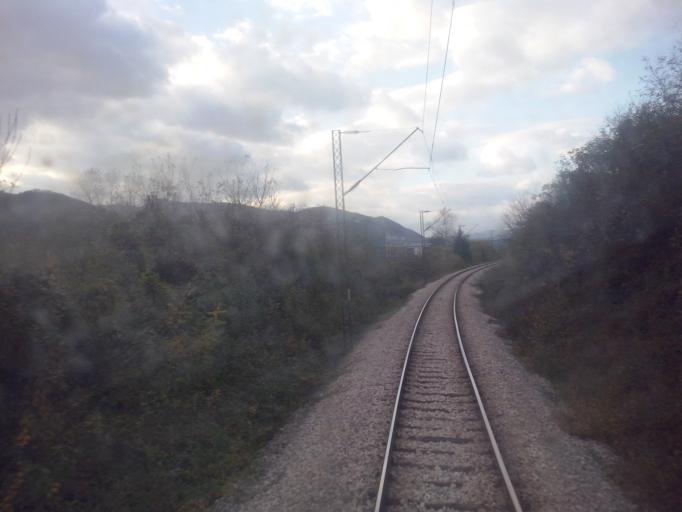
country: RS
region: Central Serbia
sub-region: Zlatiborski Okrug
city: Kosjeric
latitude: 43.9864
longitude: 19.9277
